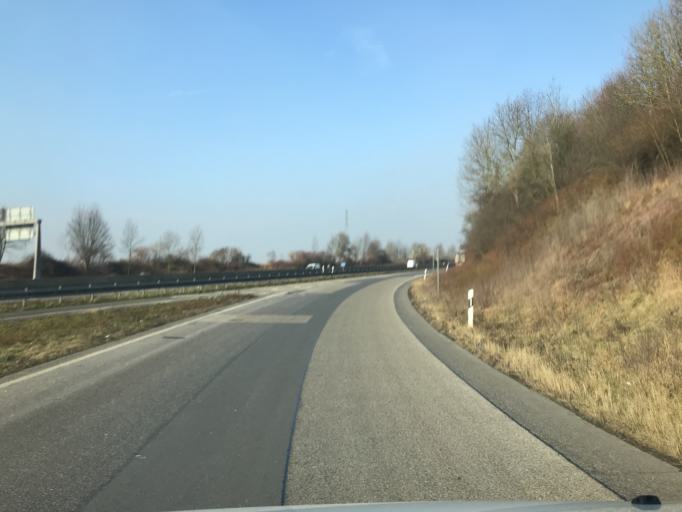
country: DE
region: North Rhine-Westphalia
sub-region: Regierungsbezirk Koln
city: Kerpen
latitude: 50.8968
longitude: 6.6945
